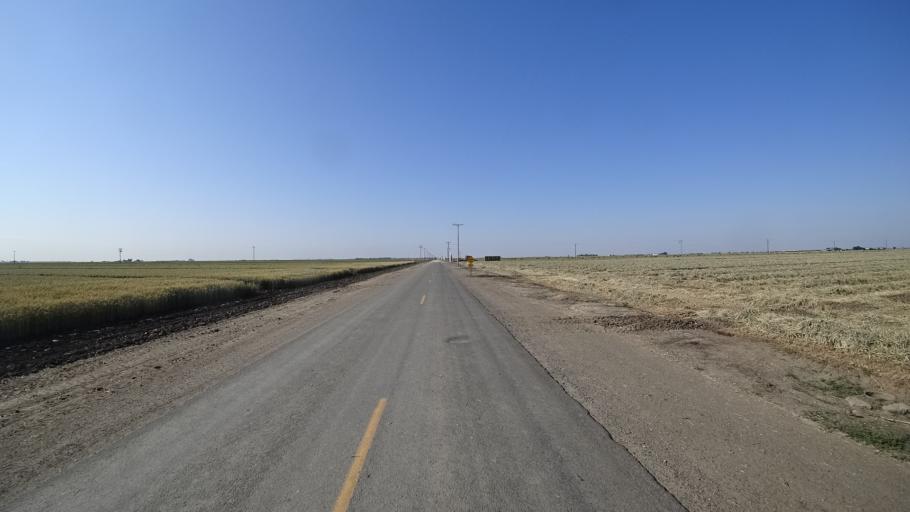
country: US
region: California
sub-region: Kings County
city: Home Garden
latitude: 36.2574
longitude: -119.5294
